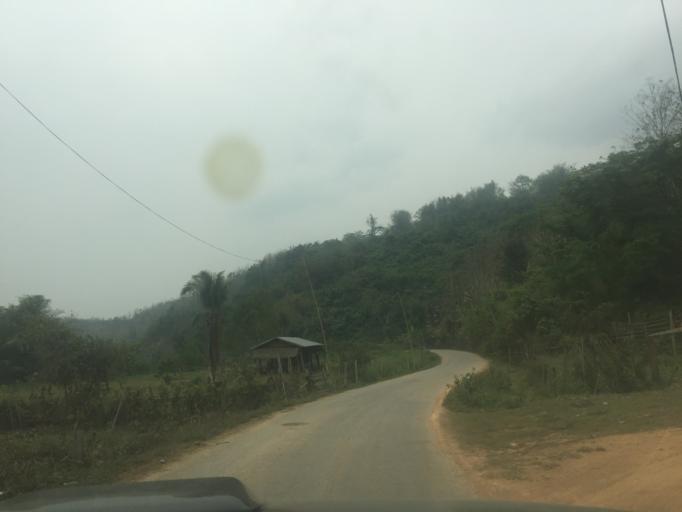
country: LA
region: Vientiane
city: Muang Sanakham
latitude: 18.3966
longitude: 101.5188
